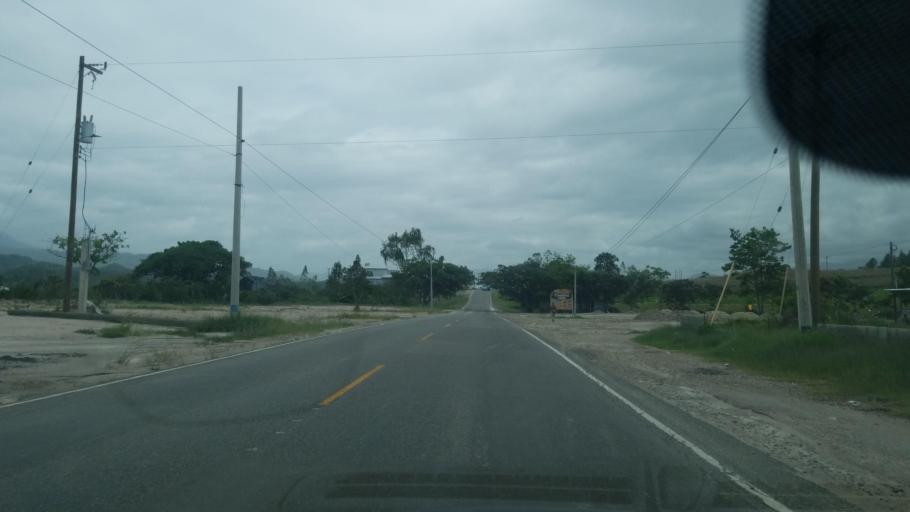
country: HN
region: Ocotepeque
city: Lucerna
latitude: 14.5452
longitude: -88.9459
